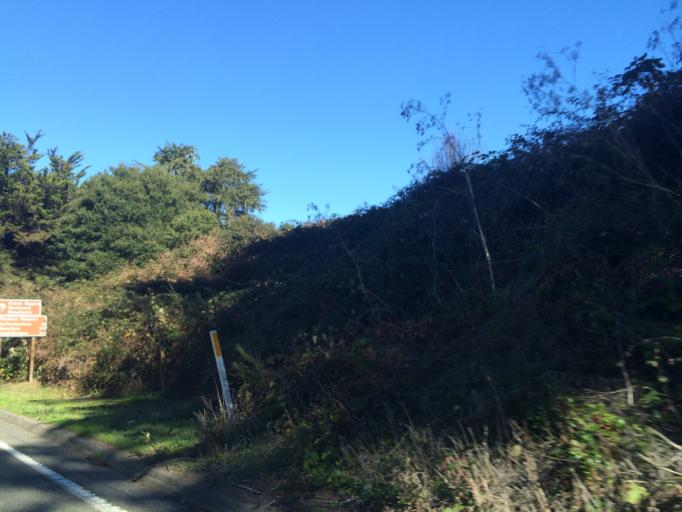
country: US
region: California
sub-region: Marin County
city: Inverness
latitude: 38.0414
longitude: -122.7884
